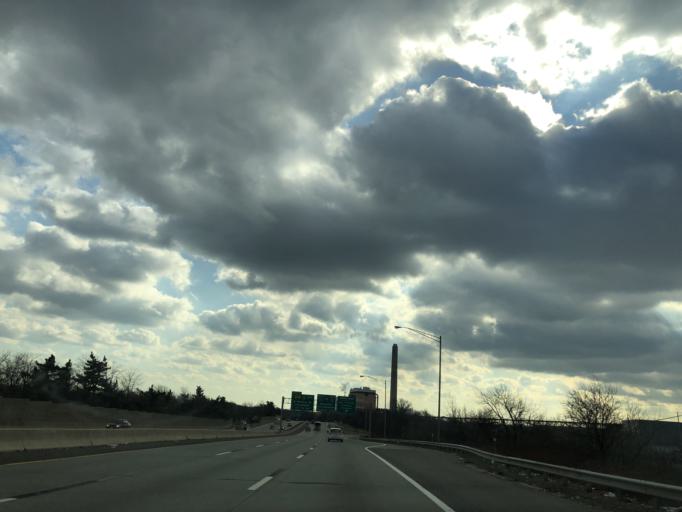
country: US
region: New Jersey
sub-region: Camden County
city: Camden
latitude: 39.9168
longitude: -75.1166
